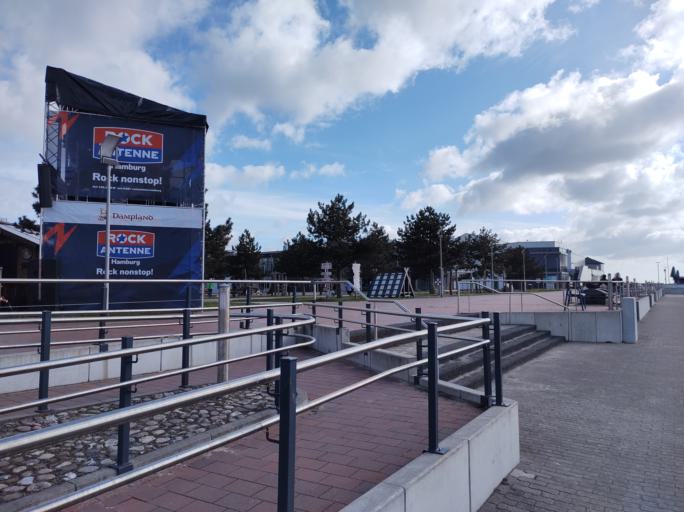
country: DE
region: Schleswig-Holstein
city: Damp
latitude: 54.5830
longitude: 10.0239
